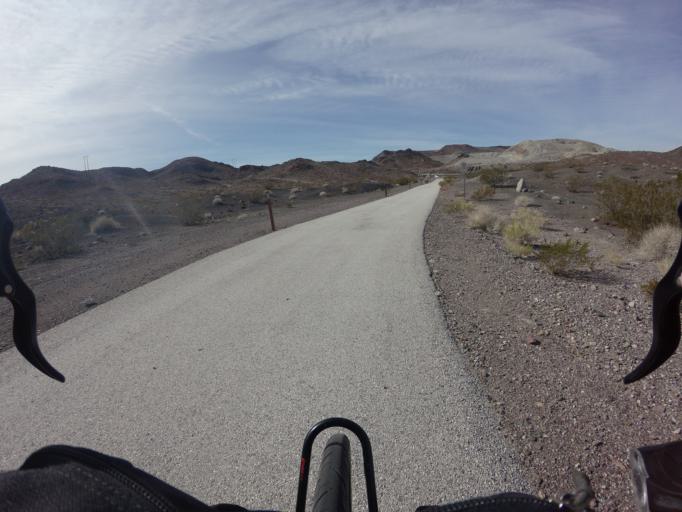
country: US
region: Nevada
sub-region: Clark County
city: Henderson
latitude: 36.0986
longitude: -114.9025
